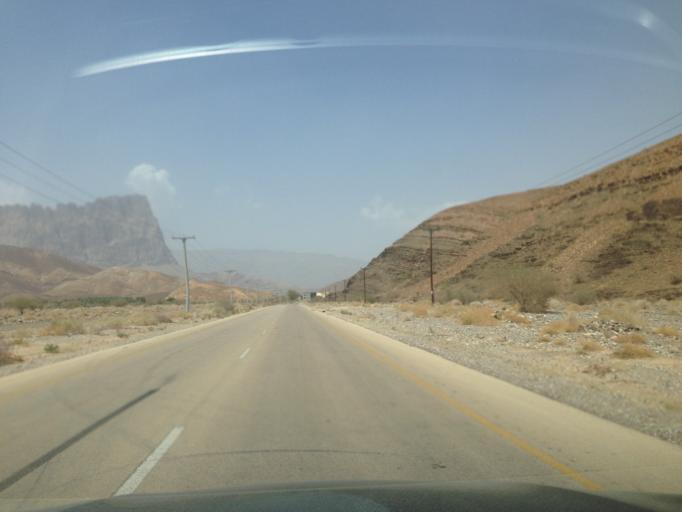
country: OM
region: Muhafazat ad Dakhiliyah
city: Bahla'
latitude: 23.2002
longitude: 56.9403
